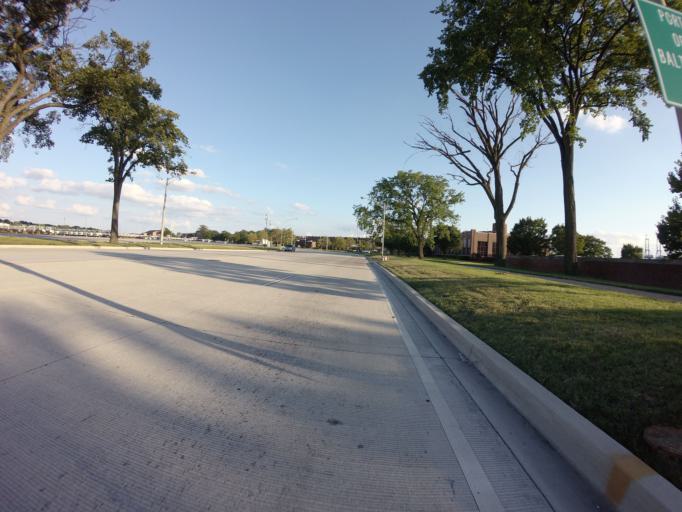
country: US
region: Maryland
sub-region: Baltimore County
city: Dundalk
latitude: 39.2634
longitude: -76.5431
